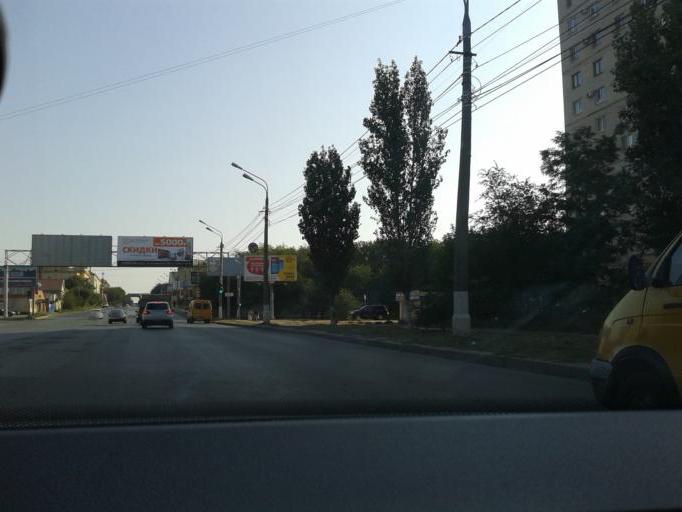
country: RU
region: Volgograd
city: Volgograd
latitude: 48.7160
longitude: 44.5012
